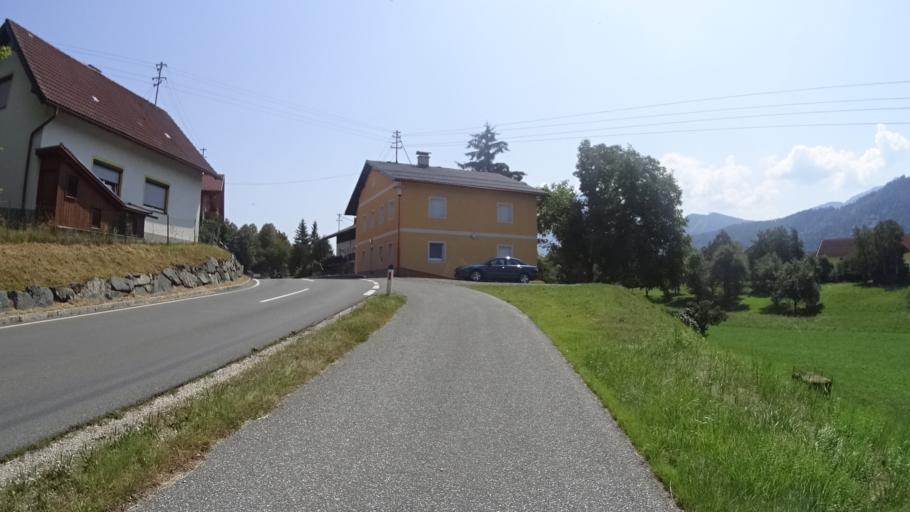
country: AT
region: Carinthia
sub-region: Politischer Bezirk Volkermarkt
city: Eberndorf
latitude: 46.5688
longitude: 14.6651
